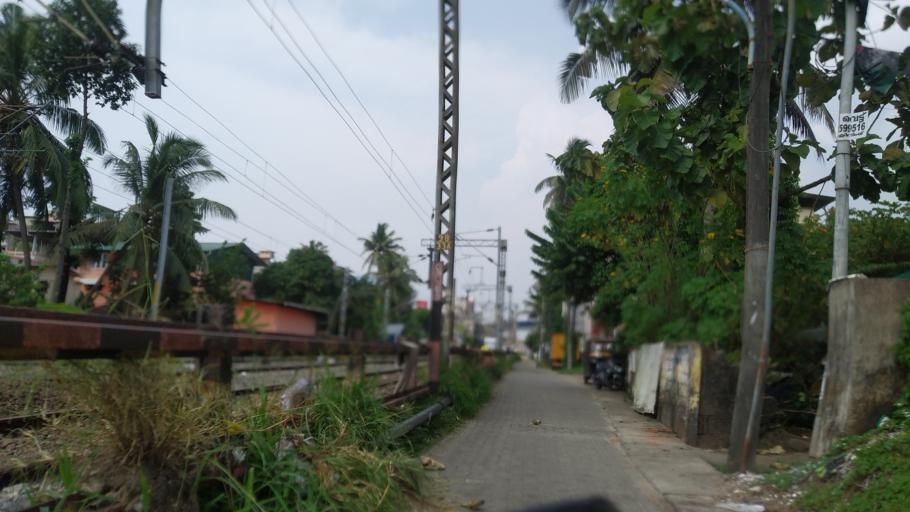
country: IN
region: Kerala
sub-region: Ernakulam
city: Cochin
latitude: 9.9621
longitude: 76.2928
